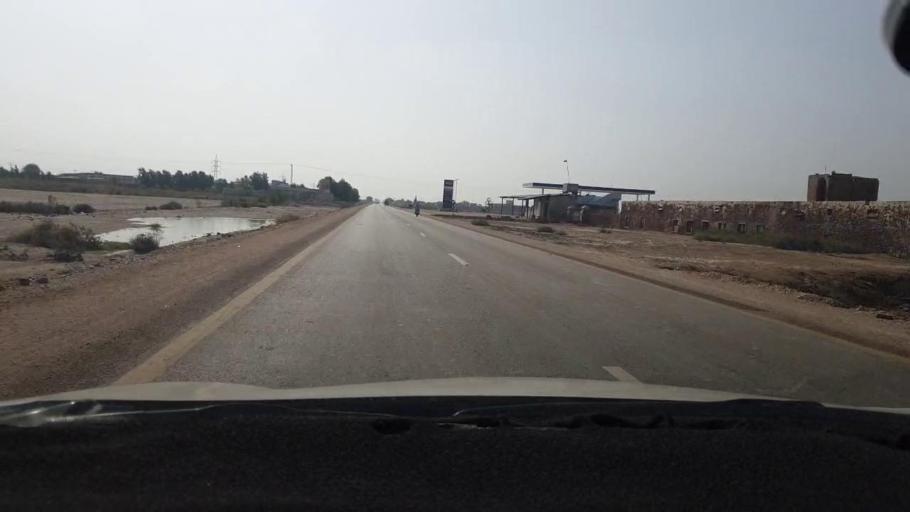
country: PK
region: Sindh
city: Jhol
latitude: 25.9224
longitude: 69.0028
